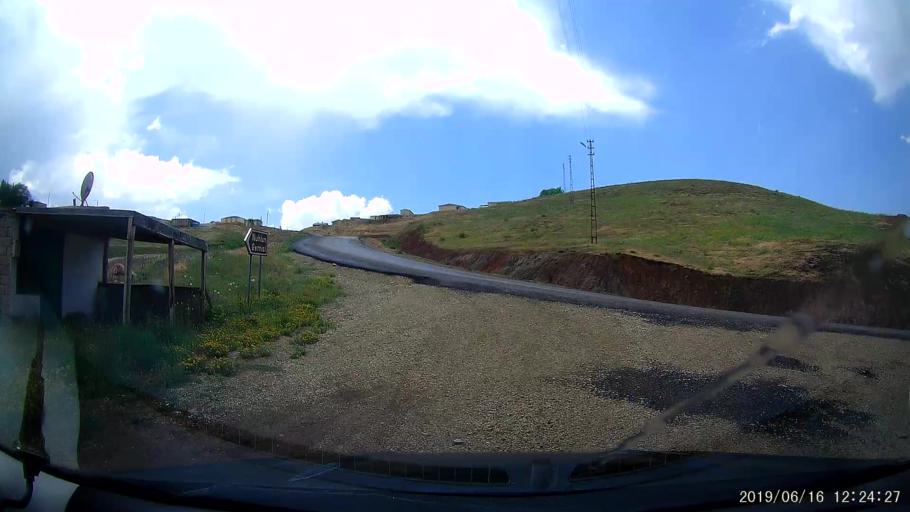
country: TR
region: Agri
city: Dogubayazit
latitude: 39.4423
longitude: 44.2333
